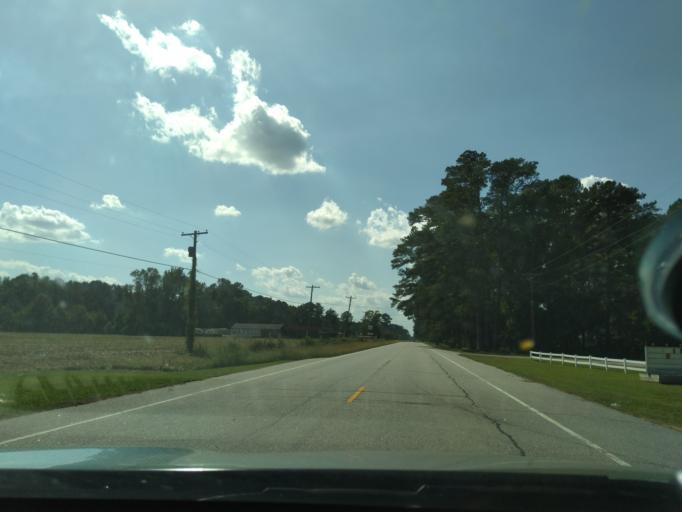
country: US
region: North Carolina
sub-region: Martin County
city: Robersonville
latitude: 35.8281
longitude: -77.2359
